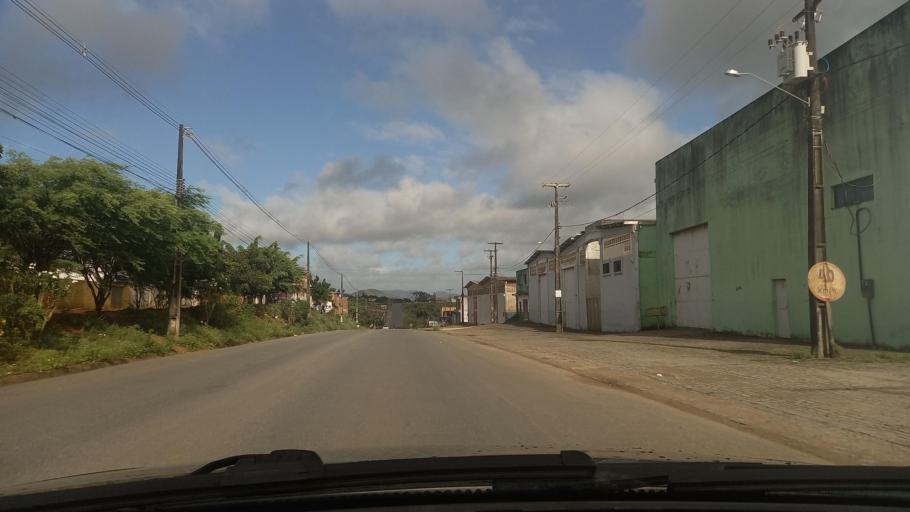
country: BR
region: Pernambuco
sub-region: Vitoria De Santo Antao
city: Vitoria de Santo Antao
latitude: -8.1226
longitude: -35.3340
